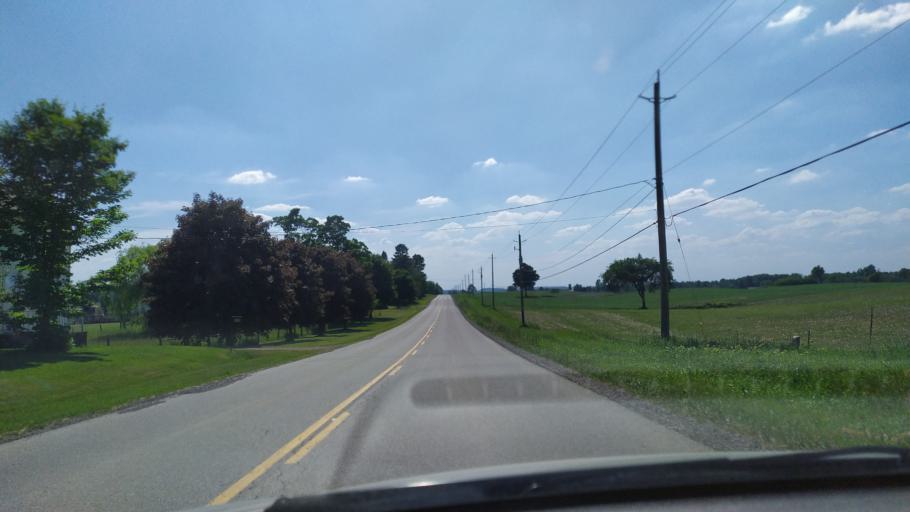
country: CA
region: Ontario
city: Kitchener
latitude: 43.3657
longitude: -80.5951
